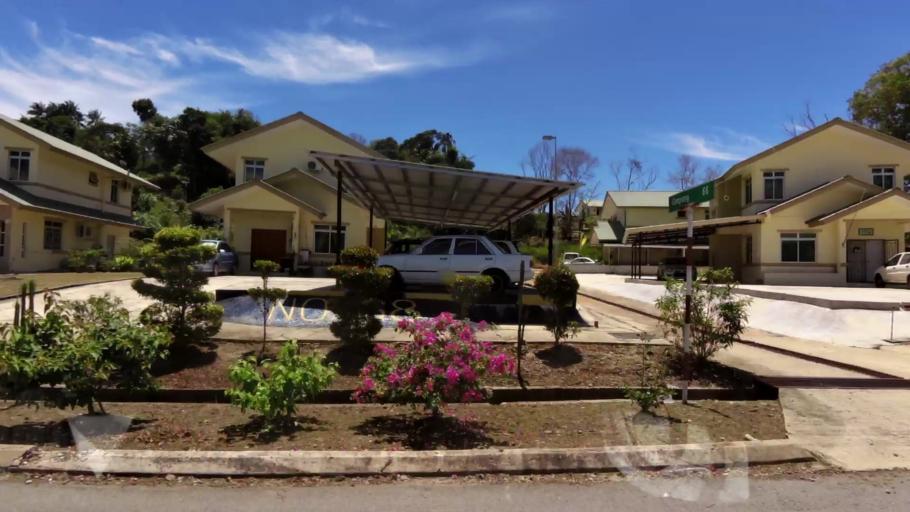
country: BN
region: Brunei and Muara
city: Bandar Seri Begawan
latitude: 5.0274
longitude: 115.0304
